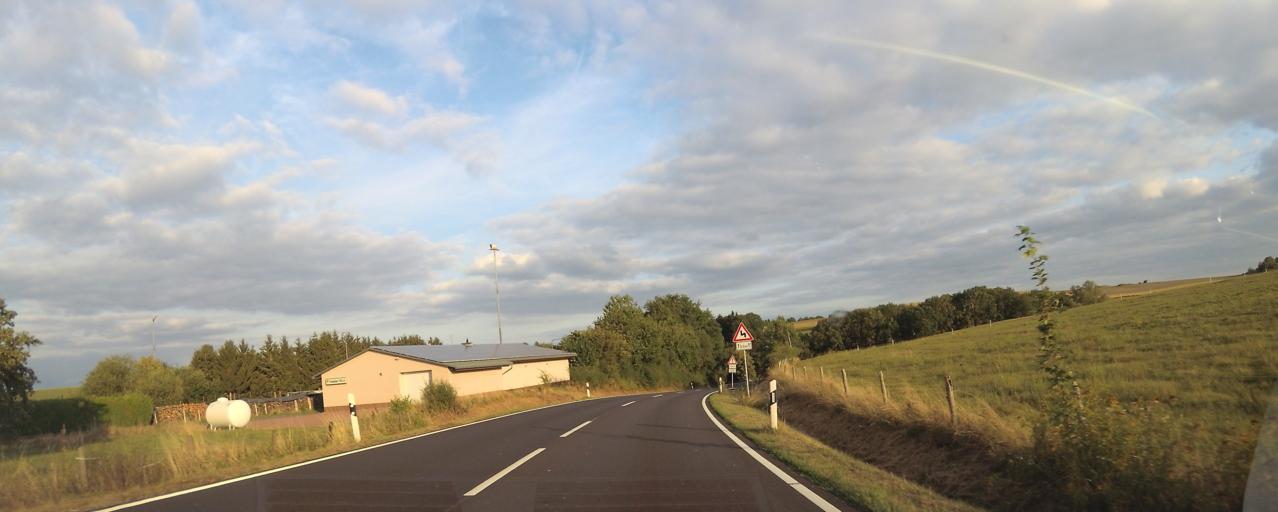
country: DE
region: Rheinland-Pfalz
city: Dudeldorf
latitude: 49.9700
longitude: 6.6377
